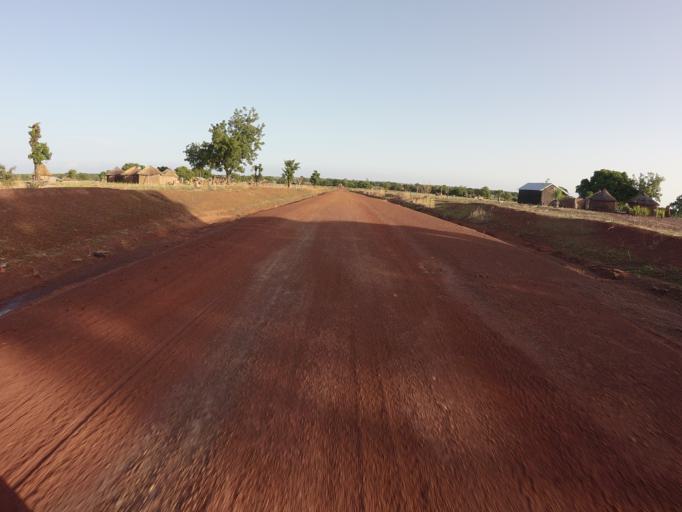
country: TG
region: Savanes
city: Sansanne-Mango
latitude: 10.3528
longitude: -0.0930
